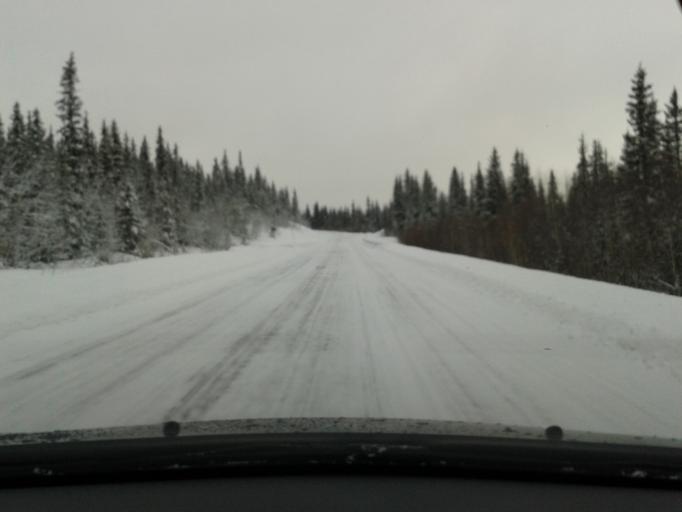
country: SE
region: Vaesterbotten
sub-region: Vilhelmina Kommun
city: Sjoberg
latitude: 65.0272
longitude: 15.8581
